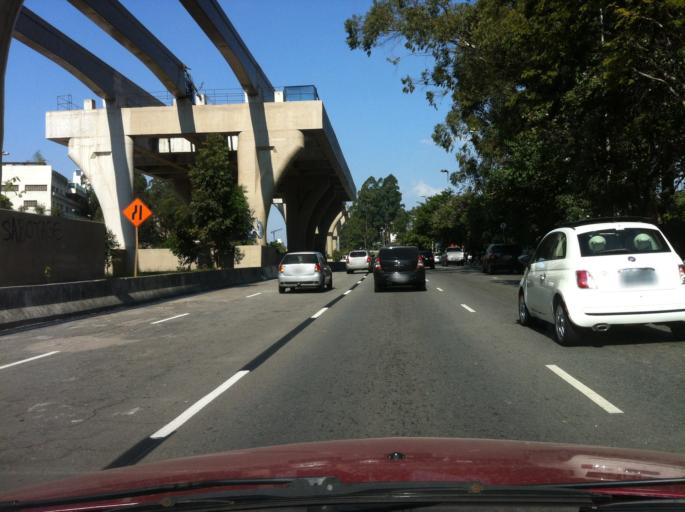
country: BR
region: Sao Paulo
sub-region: Diadema
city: Diadema
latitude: -23.6276
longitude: -46.6754
